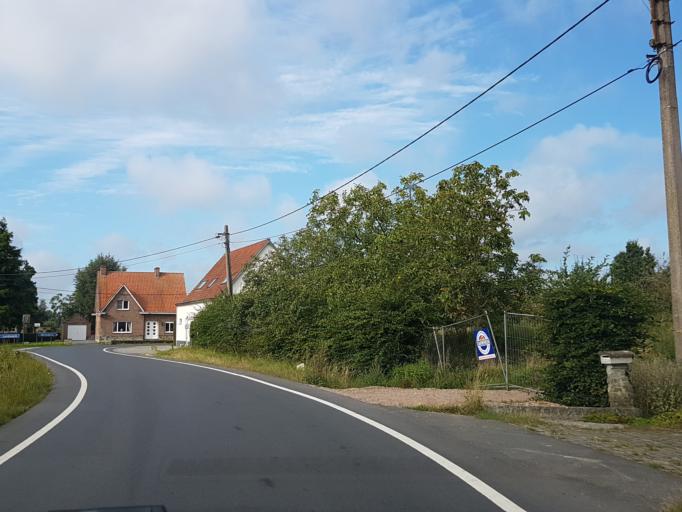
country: BE
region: Flanders
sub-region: Provincie Oost-Vlaanderen
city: Lovendegem
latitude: 51.0689
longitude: 3.6096
